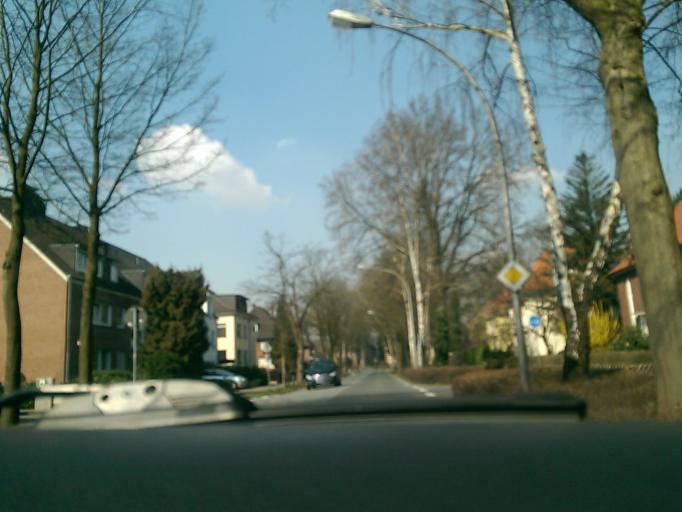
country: DE
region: North Rhine-Westphalia
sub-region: Regierungsbezirk Munster
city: Muenster
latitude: 51.9299
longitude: 7.6789
